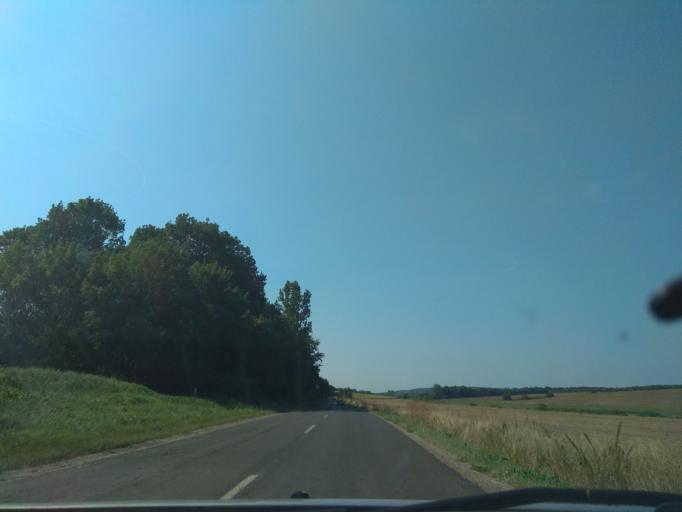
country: HU
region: Borsod-Abauj-Zemplen
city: Harsany
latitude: 47.9479
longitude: 20.7443
